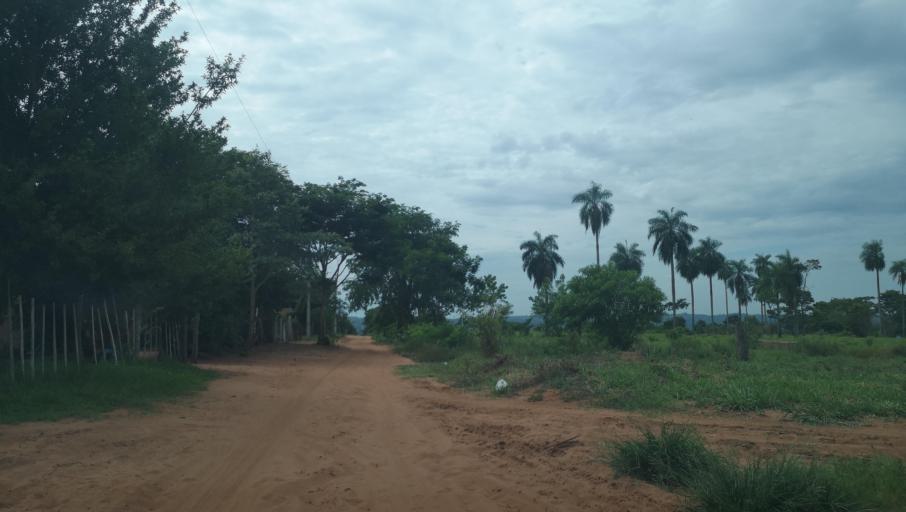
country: PY
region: San Pedro
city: Capiibary
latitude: -24.7200
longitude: -56.0102
